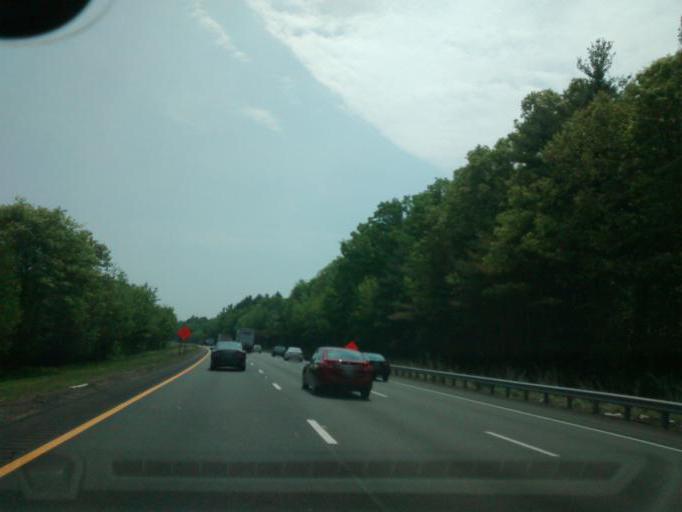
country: US
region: Massachusetts
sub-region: Norfolk County
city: Bellingham
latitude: 42.1064
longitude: -71.4568
